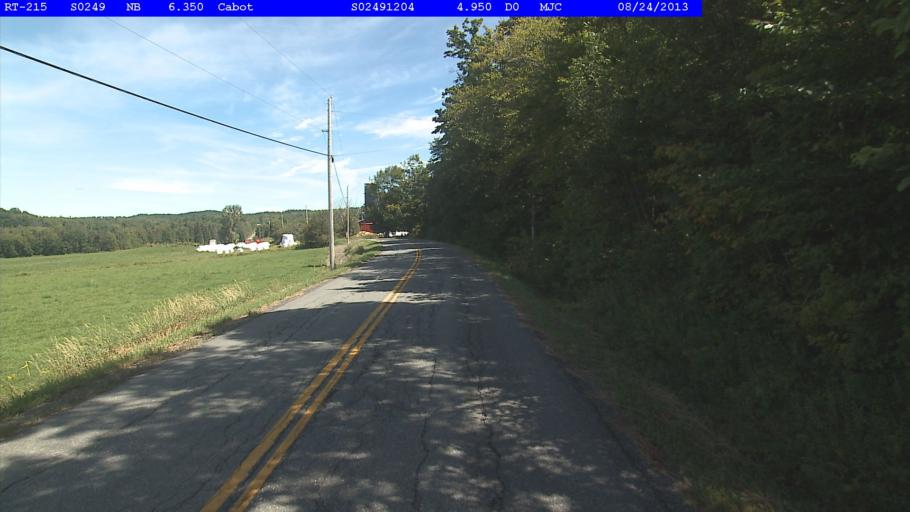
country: US
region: Vermont
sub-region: Caledonia County
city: Hardwick
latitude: 44.4251
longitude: -72.2938
